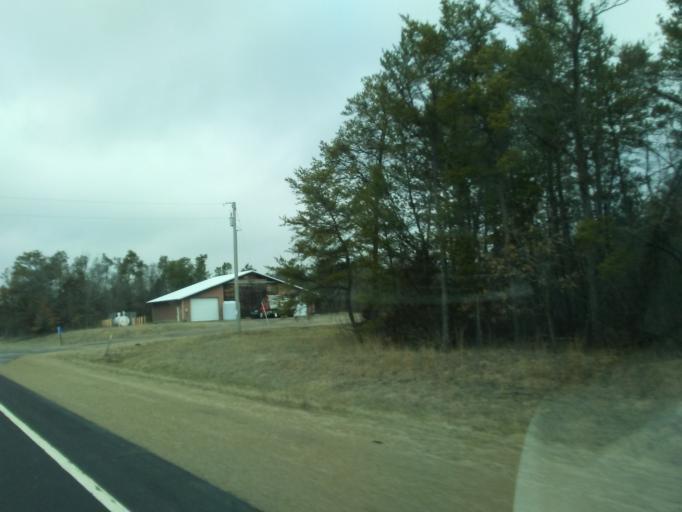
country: US
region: Wisconsin
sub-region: Richland County
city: Richland Center
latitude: 43.2164
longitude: -90.2853
